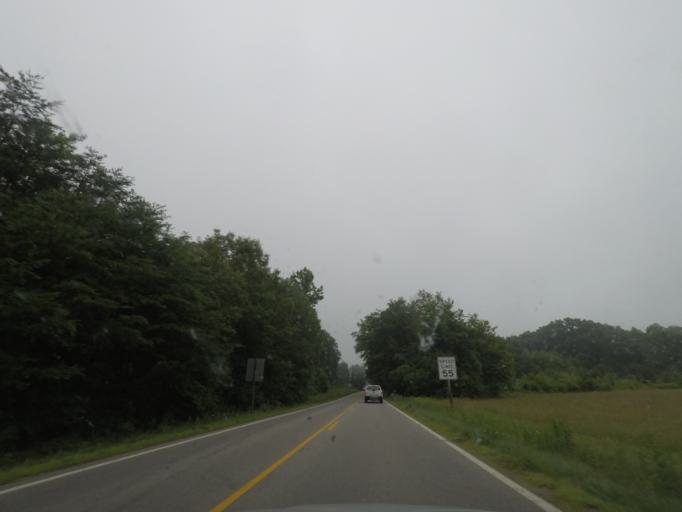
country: US
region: Virginia
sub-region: Prince Edward County
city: Farmville
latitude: 37.3199
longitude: -78.4618
